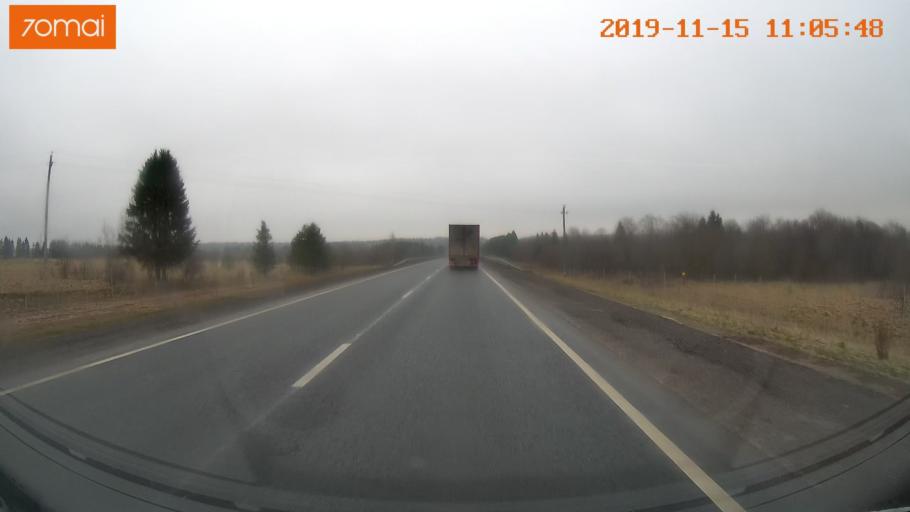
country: RU
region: Vologda
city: Chebsara
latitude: 59.1187
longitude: 39.0118
